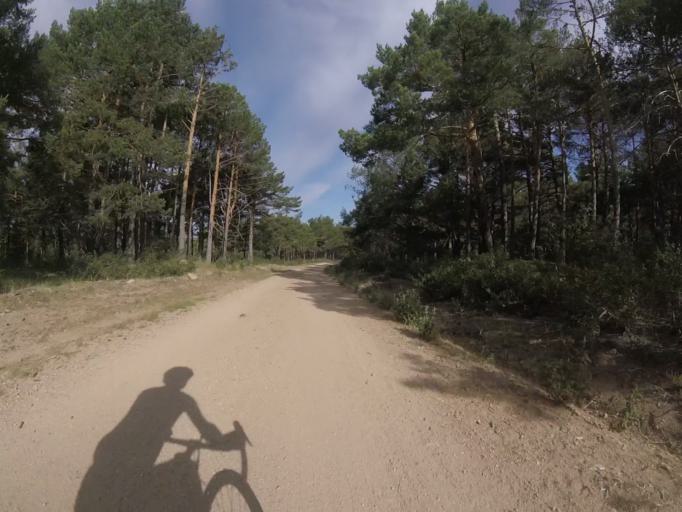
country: ES
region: Castille and Leon
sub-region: Provincia de Avila
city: Peguerinos
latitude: 40.6541
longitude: -4.1829
